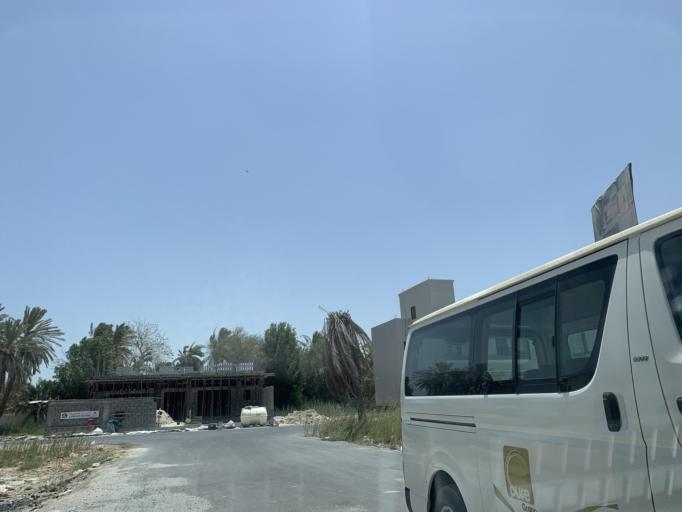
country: BH
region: Manama
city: Jidd Hafs
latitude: 26.2255
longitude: 50.4717
